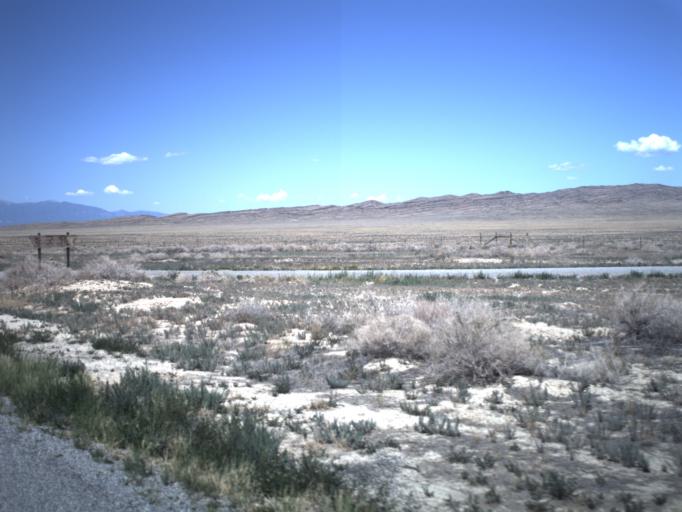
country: US
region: Utah
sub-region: Beaver County
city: Milford
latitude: 39.0601
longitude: -113.7570
